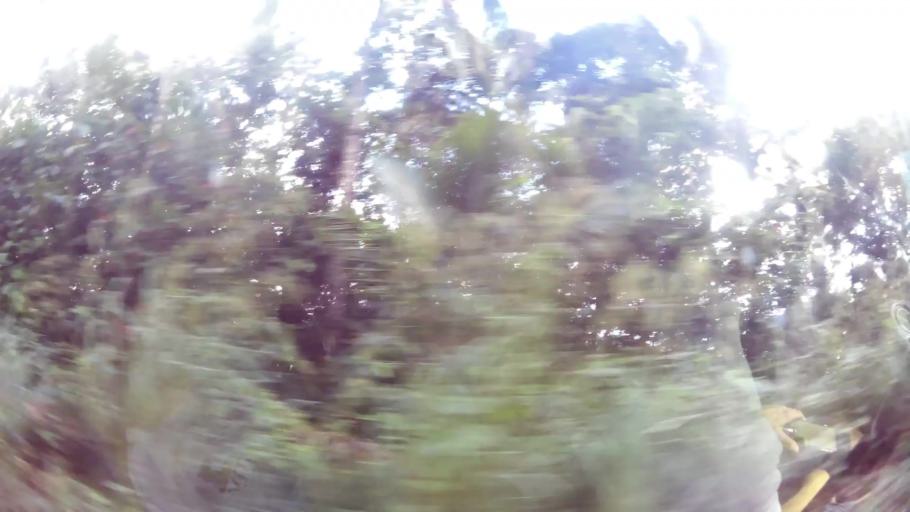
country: DM
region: Saint Andrew
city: Calibishie
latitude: 15.5919
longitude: -61.3683
